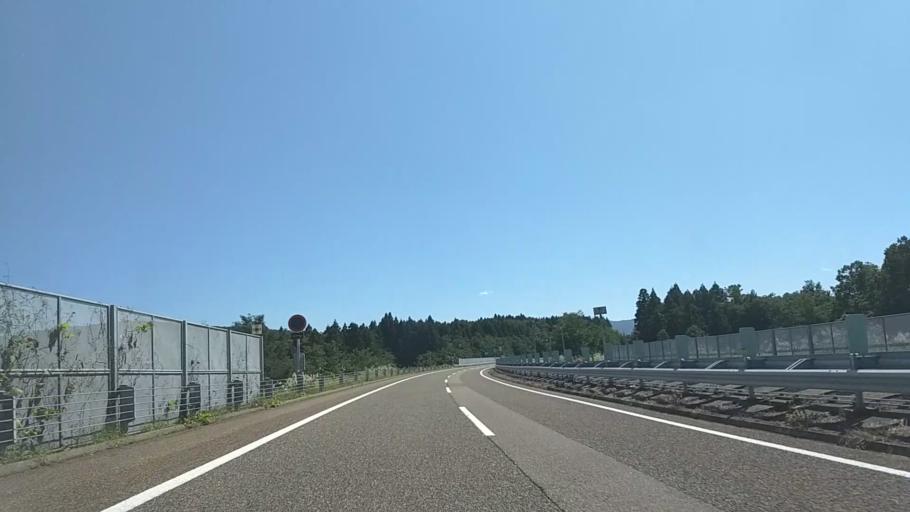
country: JP
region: Niigata
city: Arai
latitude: 36.9783
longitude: 138.2206
